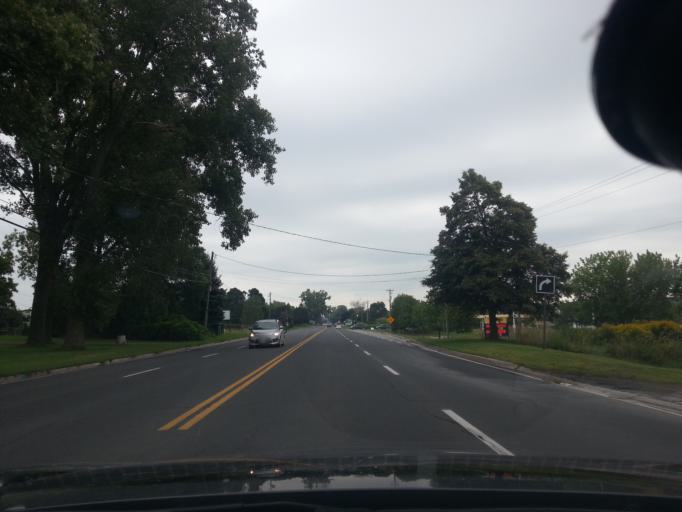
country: CA
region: Ontario
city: Picton
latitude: 43.9995
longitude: -77.1628
